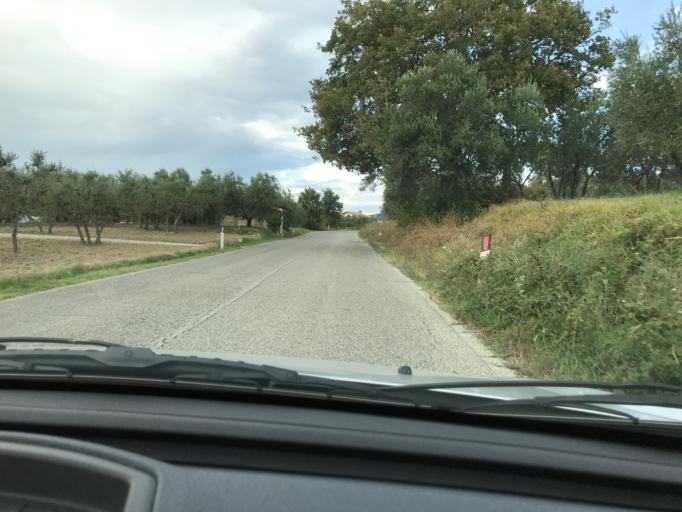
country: IT
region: Umbria
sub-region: Provincia di Terni
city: Montecchio
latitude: 42.6570
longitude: 12.2782
